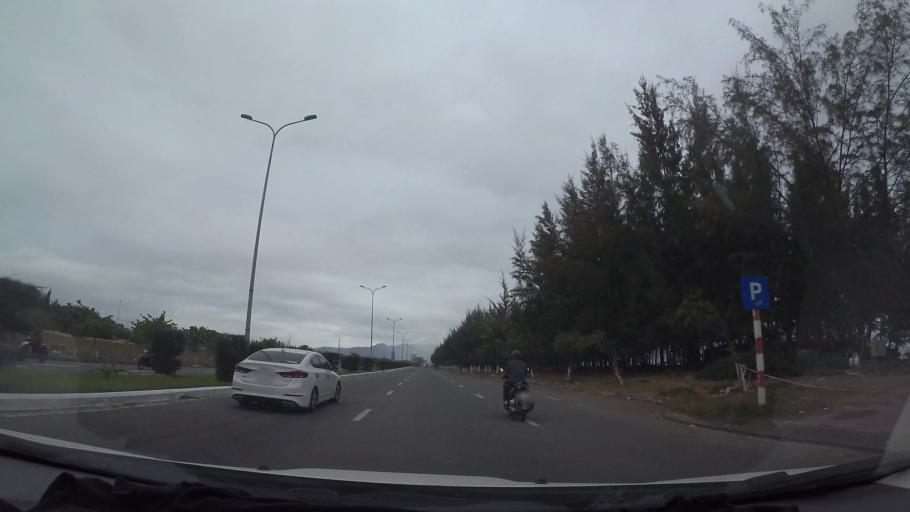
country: VN
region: Da Nang
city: Lien Chieu
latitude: 16.0965
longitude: 108.1447
